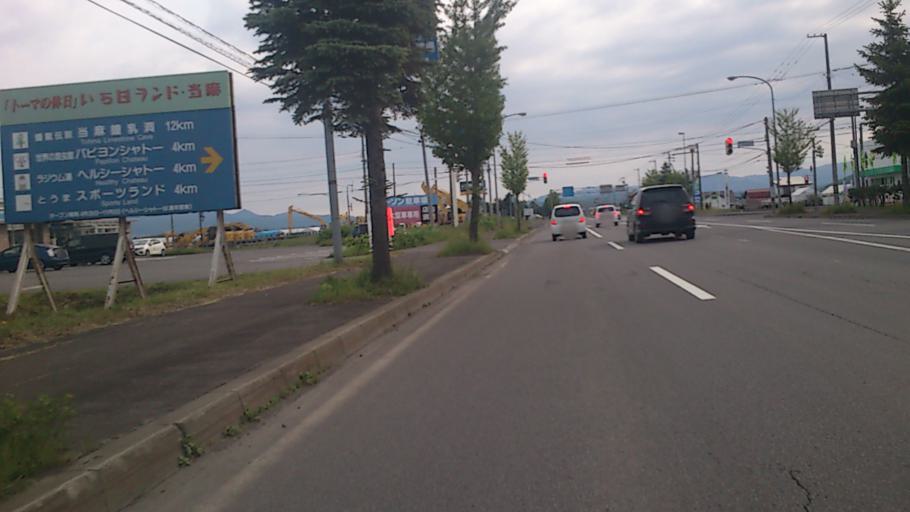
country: JP
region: Hokkaido
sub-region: Asahikawa-shi
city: Asahikawa
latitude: 43.8445
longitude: 142.4884
